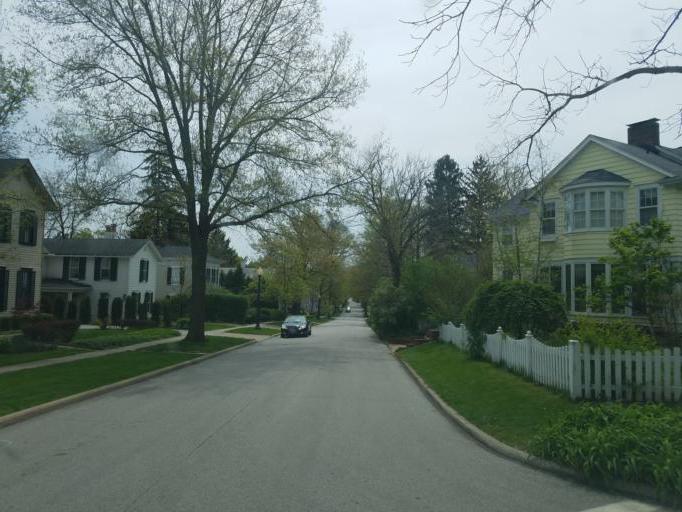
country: US
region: Ohio
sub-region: Summit County
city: Hudson
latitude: 41.2430
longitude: -81.4376
